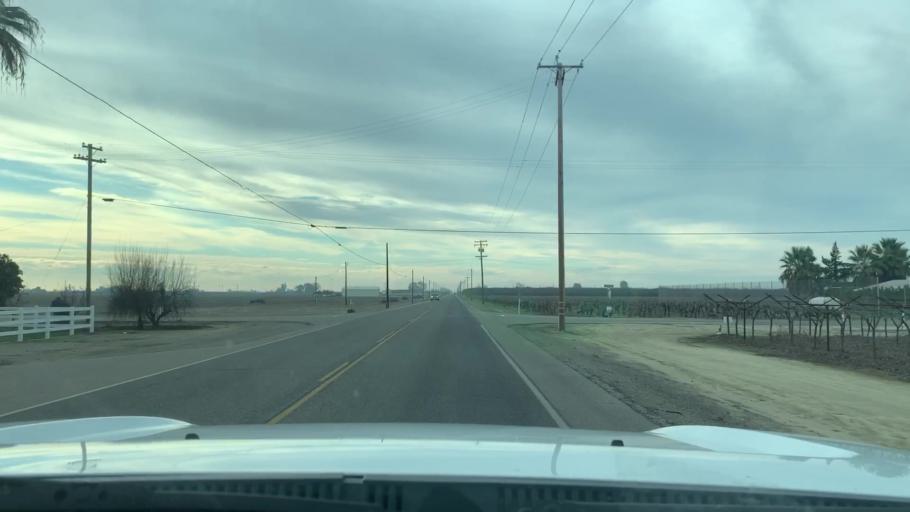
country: US
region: California
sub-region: Fresno County
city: Easton
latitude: 36.6054
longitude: -119.7634
